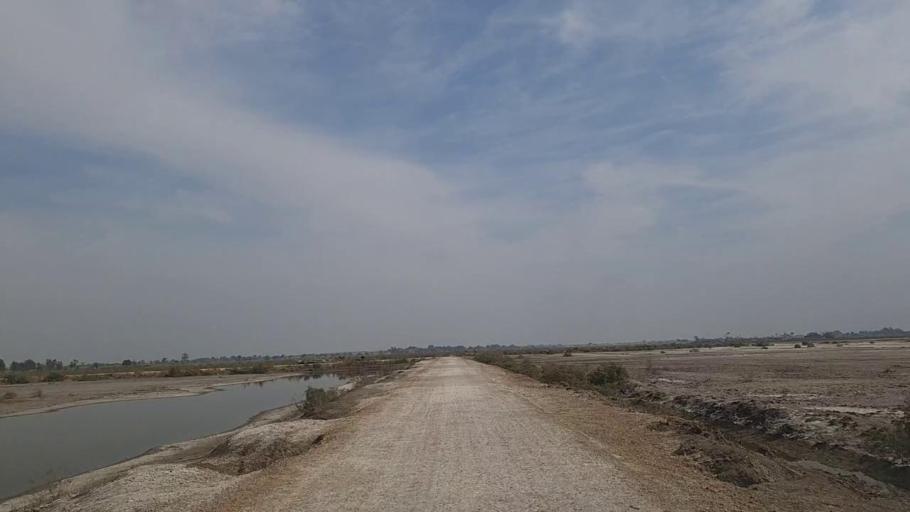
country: PK
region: Sindh
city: Daur
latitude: 26.4784
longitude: 68.4039
